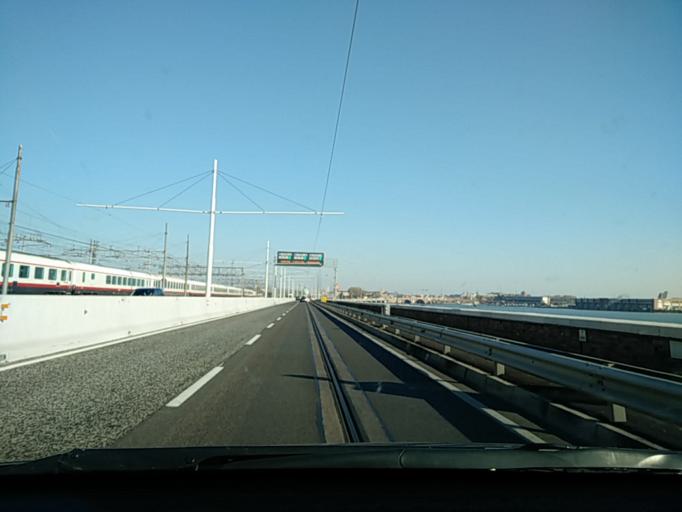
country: IT
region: Veneto
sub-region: Provincia di Venezia
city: Venice
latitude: 45.4491
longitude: 12.3068
